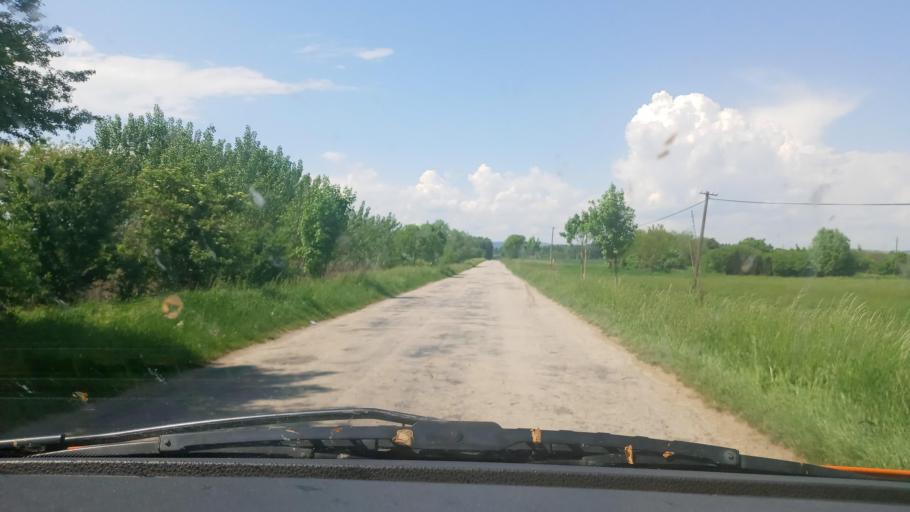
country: HU
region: Baranya
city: Siklos
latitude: 45.8048
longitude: 18.3445
